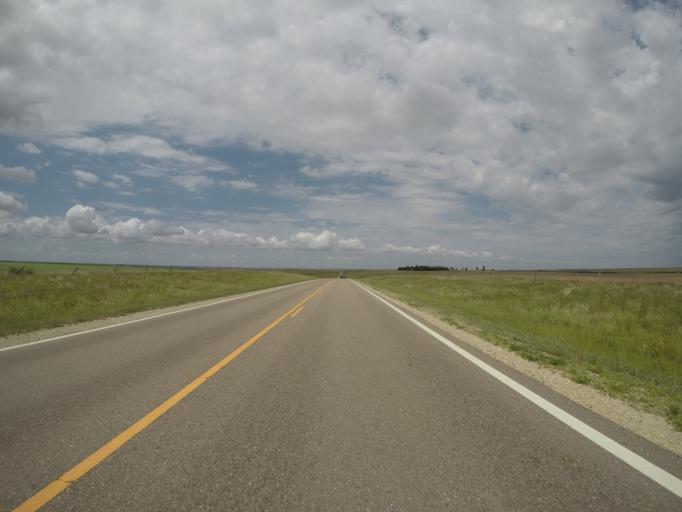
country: US
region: Kansas
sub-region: Rawlins County
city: Atwood
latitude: 39.7673
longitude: -101.0470
